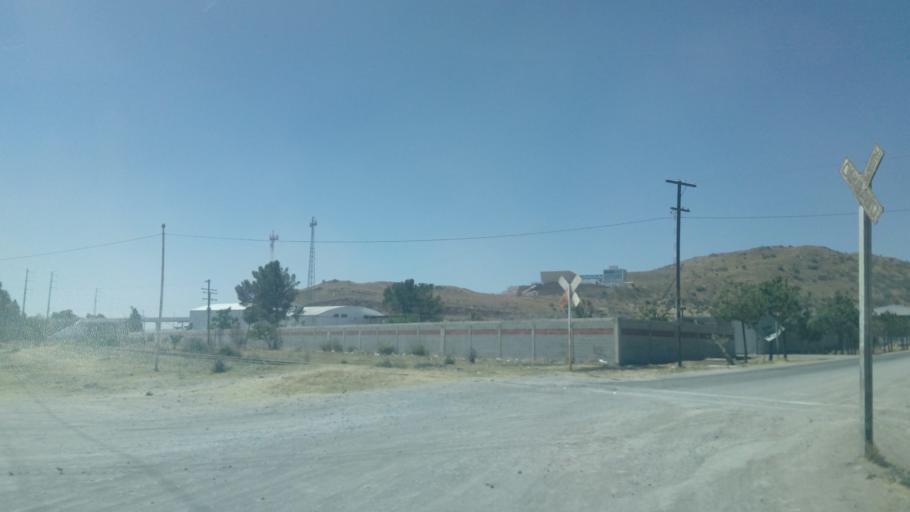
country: MX
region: Durango
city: Victoria de Durango
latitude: 24.0734
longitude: -104.6564
